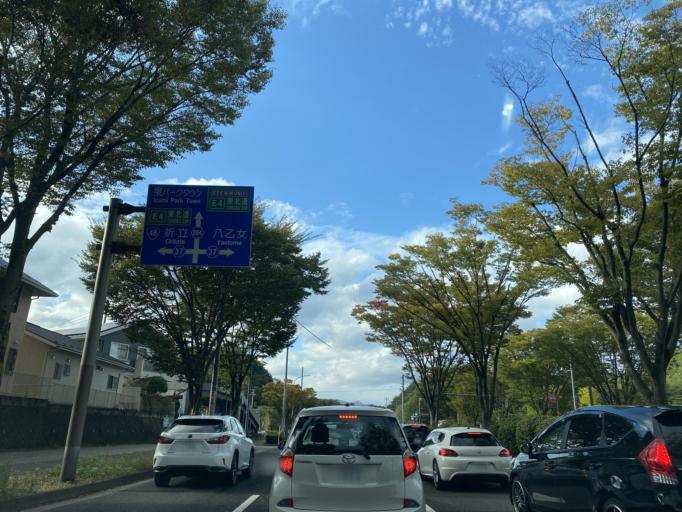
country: JP
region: Miyagi
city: Sendai-shi
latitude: 38.3096
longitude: 140.8486
